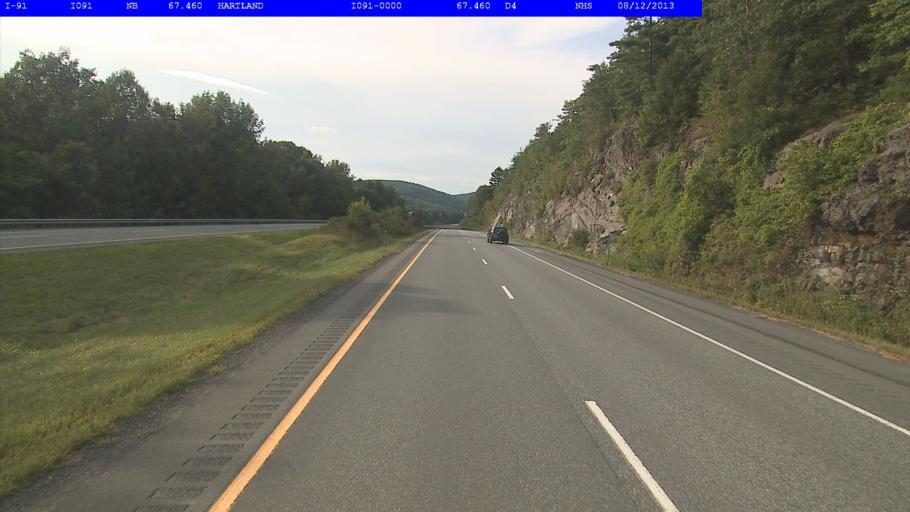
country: US
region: Vermont
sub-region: Windsor County
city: White River Junction
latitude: 43.6078
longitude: -72.3423
